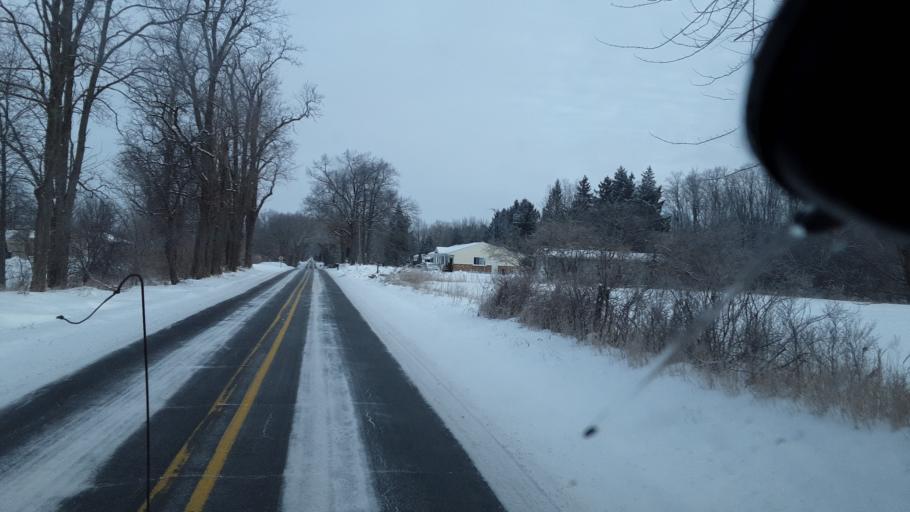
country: US
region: Michigan
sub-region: Jackson County
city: Jackson
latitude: 42.3025
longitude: -84.4829
